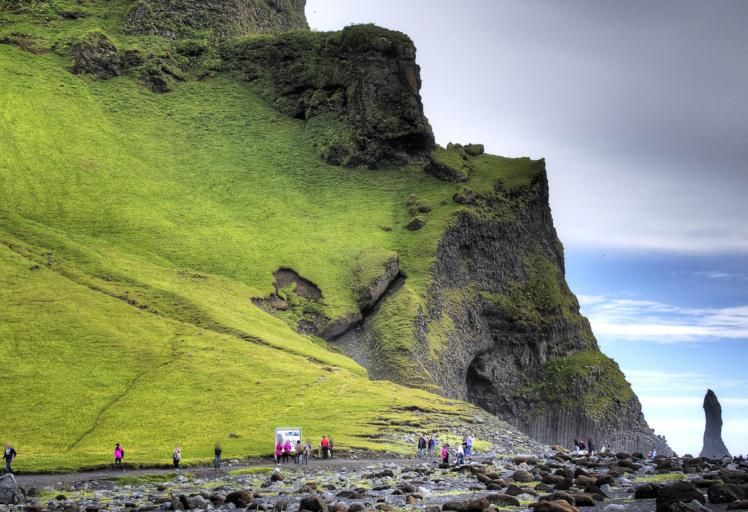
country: IS
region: South
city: Vestmannaeyjar
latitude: 63.4041
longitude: -19.0451
